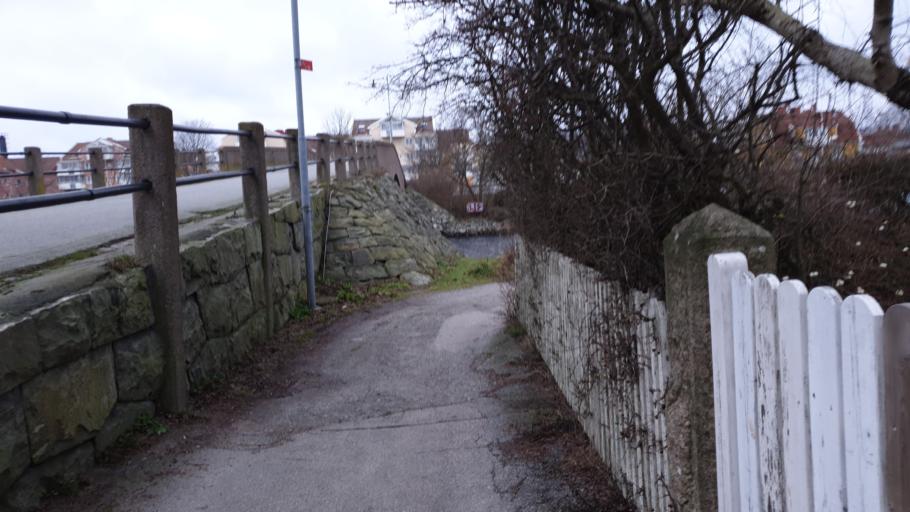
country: SE
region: Blekinge
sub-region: Karlskrona Kommun
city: Karlskrona
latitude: 56.1650
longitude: 15.5712
